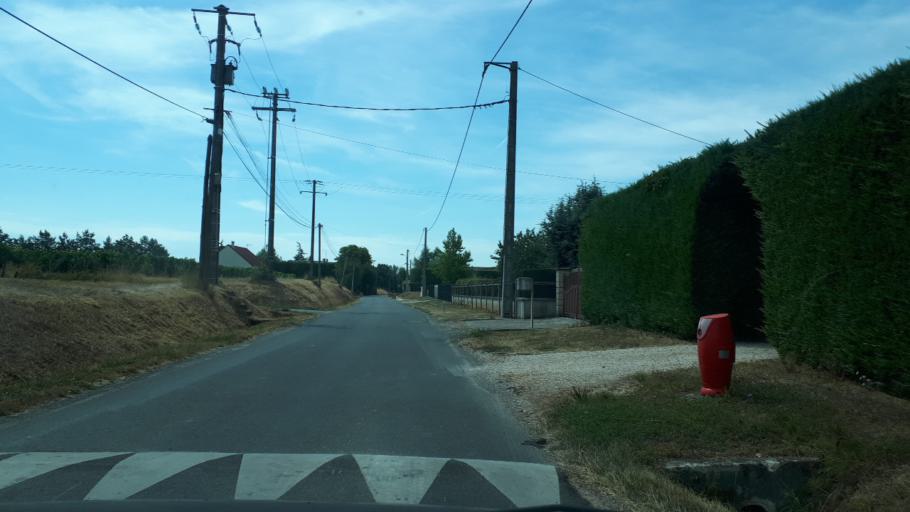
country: FR
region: Centre
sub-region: Departement du Loir-et-Cher
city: Contres
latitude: 47.3953
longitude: 1.3782
